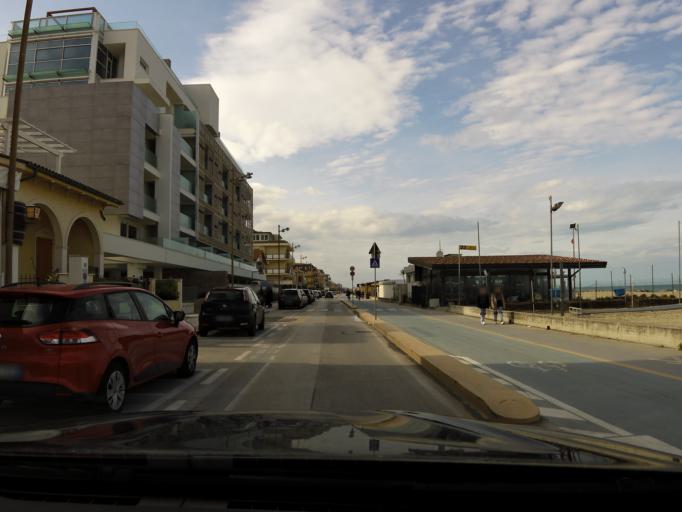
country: IT
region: The Marches
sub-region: Provincia di Macerata
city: Civitanova Marche
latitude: 43.3210
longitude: 13.7199
